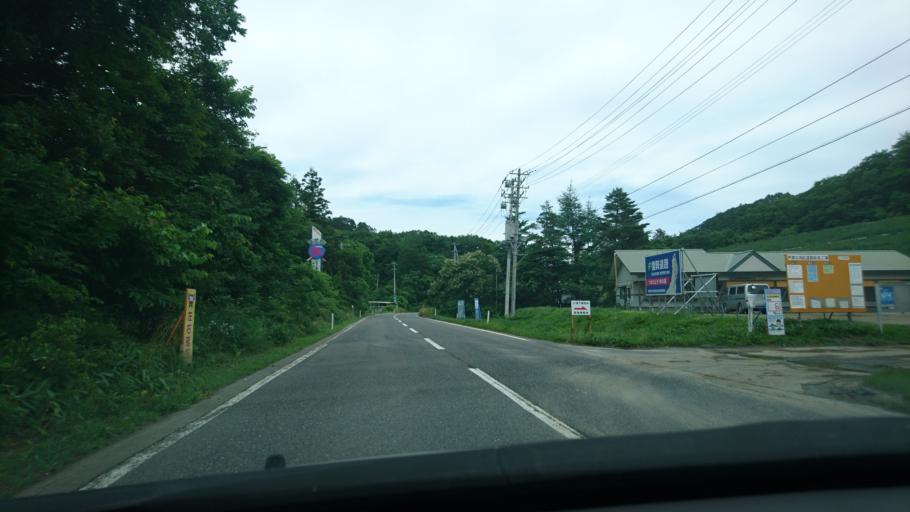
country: JP
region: Iwate
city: Miyako
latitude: 39.9808
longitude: 141.8580
